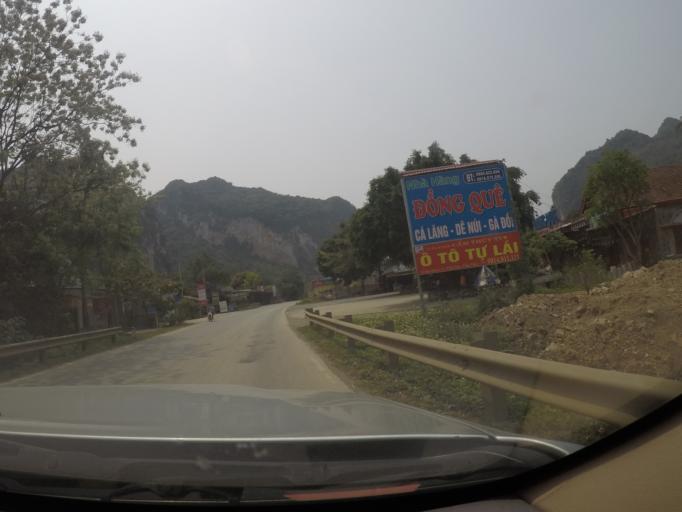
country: VN
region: Thanh Hoa
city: Thi Tran Cam Thuy
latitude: 20.2206
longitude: 105.4912
